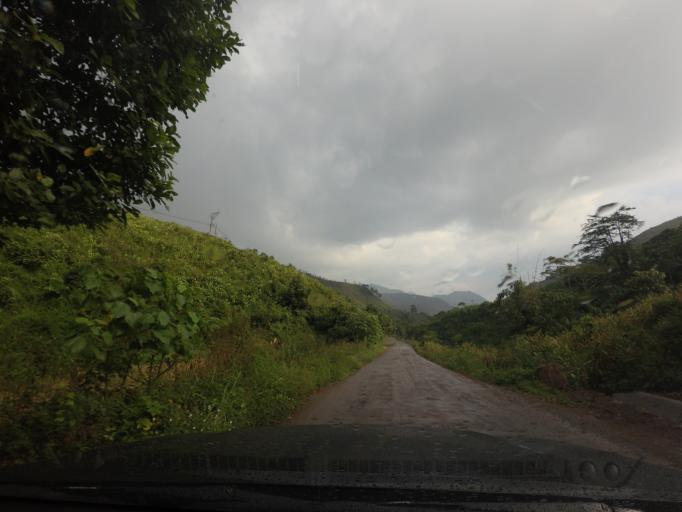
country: TH
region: Nan
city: Bo Kluea
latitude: 19.2973
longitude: 101.1741
